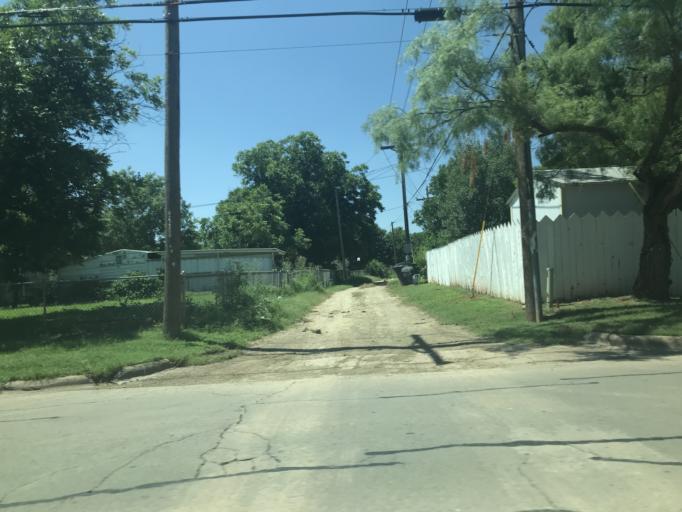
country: US
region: Texas
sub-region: Taylor County
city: Abilene
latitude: 32.4632
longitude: -99.7538
